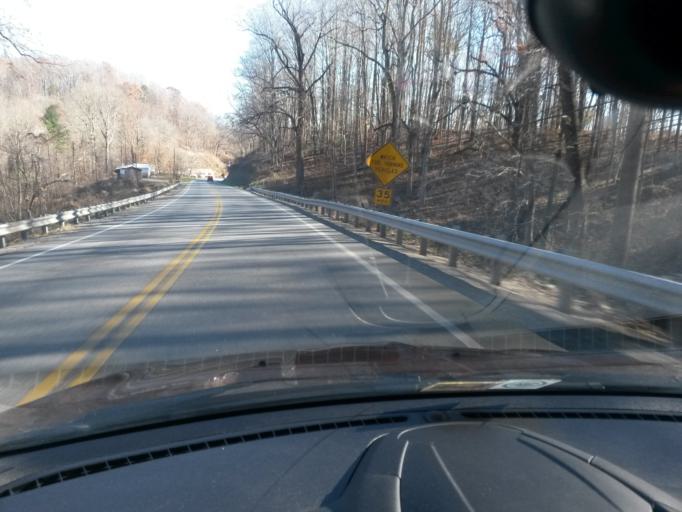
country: US
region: Virginia
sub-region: Henry County
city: Bassett
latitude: 36.7608
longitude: -80.0161
